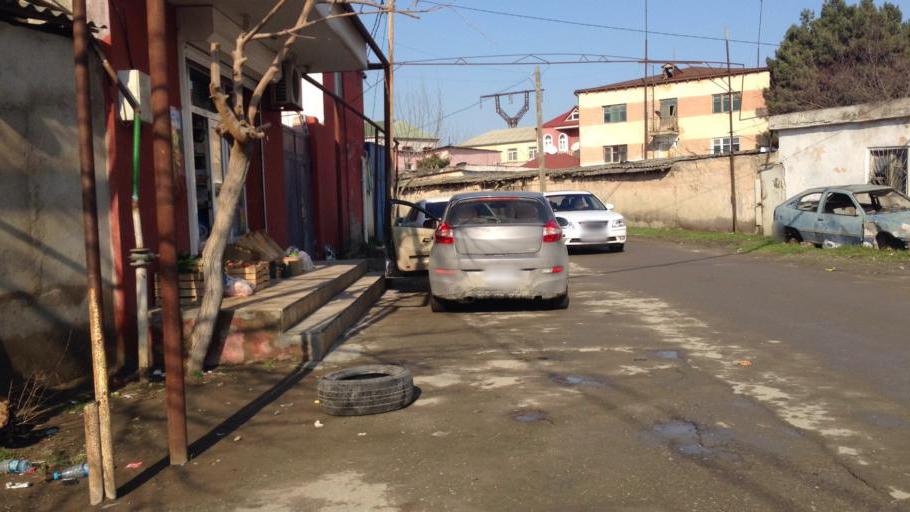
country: AZ
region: Baki
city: Binagadi
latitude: 40.4344
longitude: 49.8540
